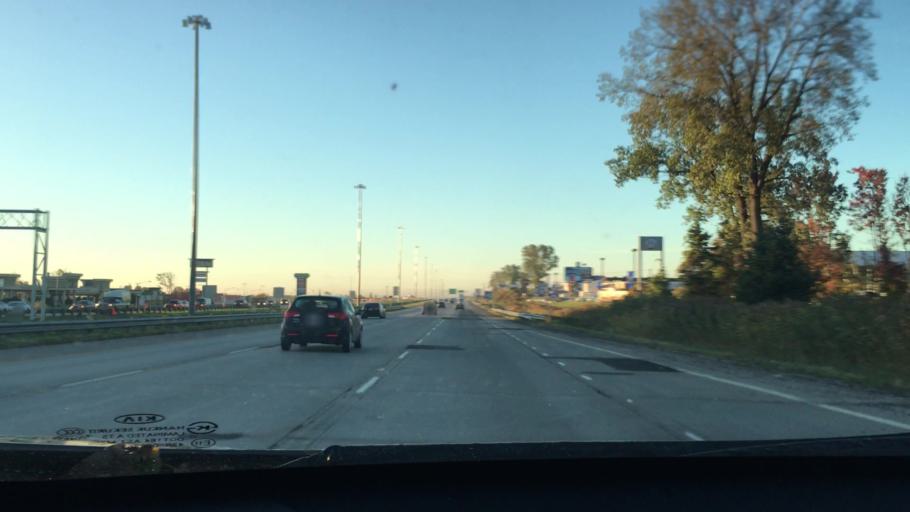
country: CA
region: Quebec
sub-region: Laurentides
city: Saint-Jerome
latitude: 45.7728
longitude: -74.0209
